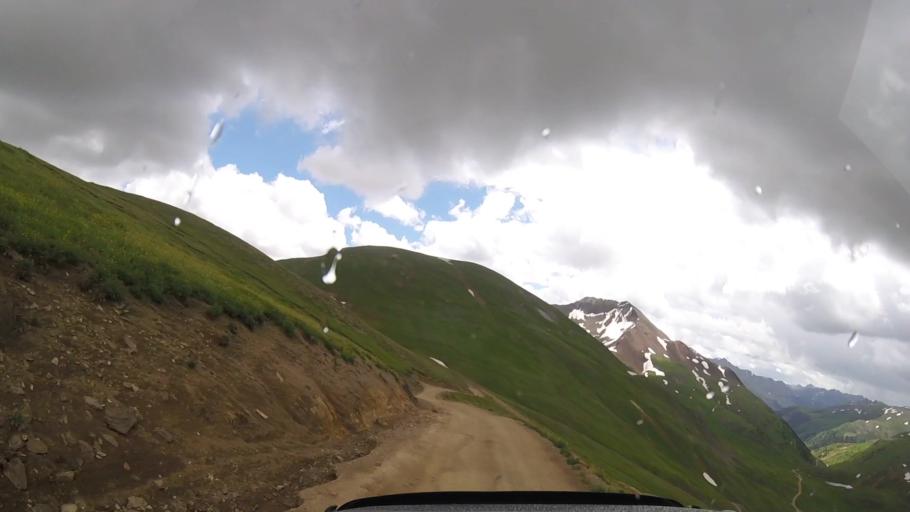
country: US
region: Colorado
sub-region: Ouray County
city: Ouray
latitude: 37.9646
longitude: -107.5764
